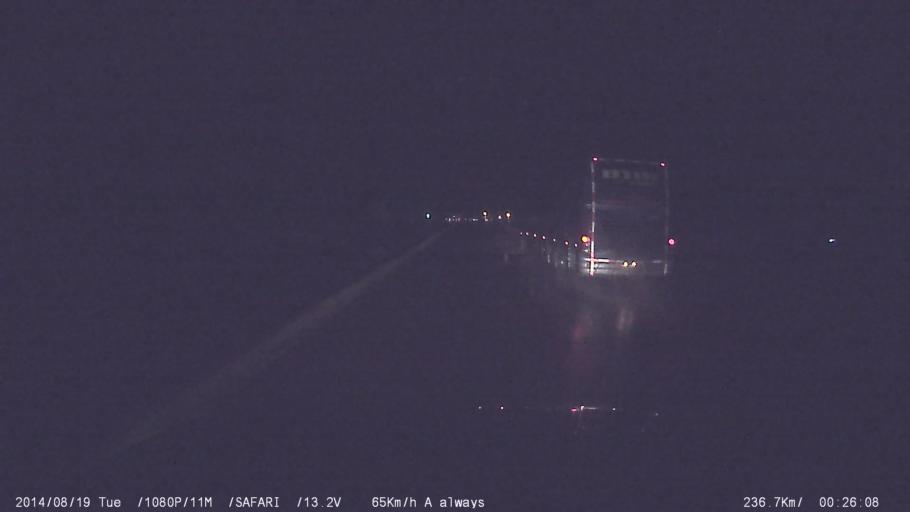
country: IN
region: Kerala
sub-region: Palakkad district
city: Chittur
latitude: 10.7982
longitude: 76.7759
